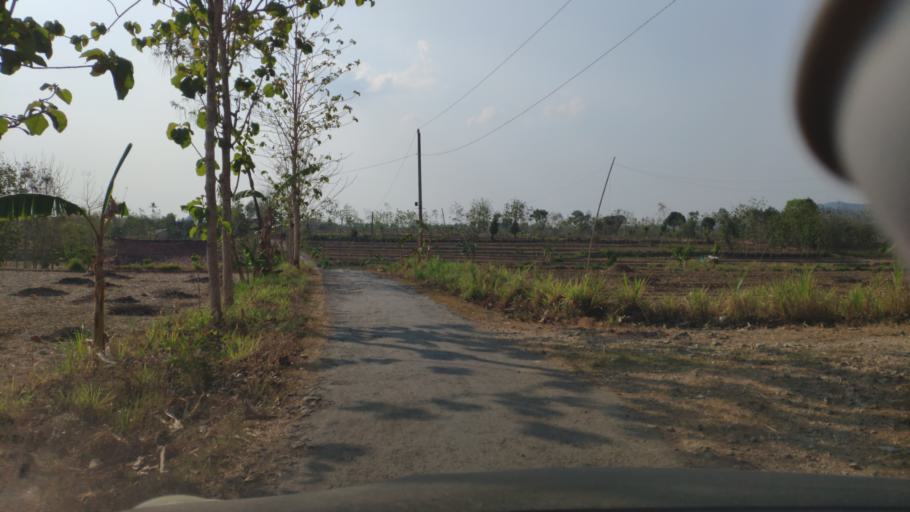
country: ID
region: Central Java
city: Bogorejo
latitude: -6.9403
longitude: 111.5149
